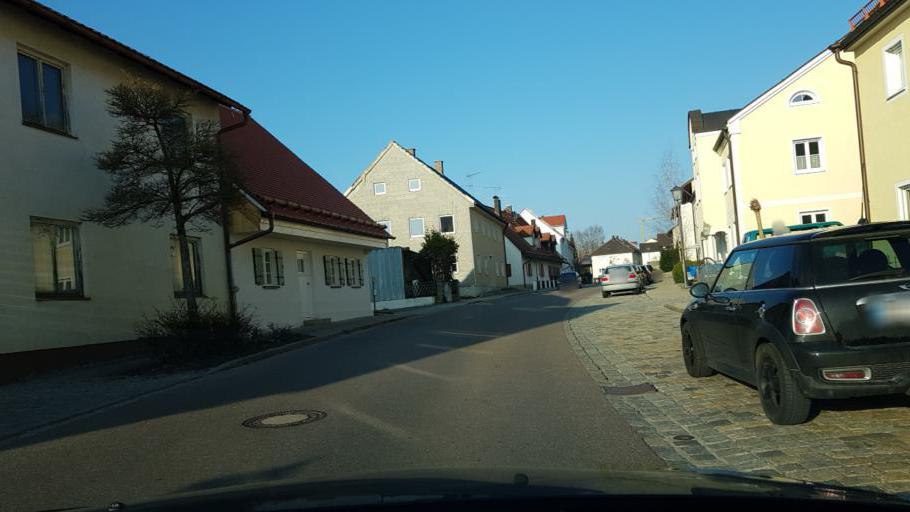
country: DE
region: Bavaria
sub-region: Upper Bavaria
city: Altomunster
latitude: 48.3898
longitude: 11.2569
